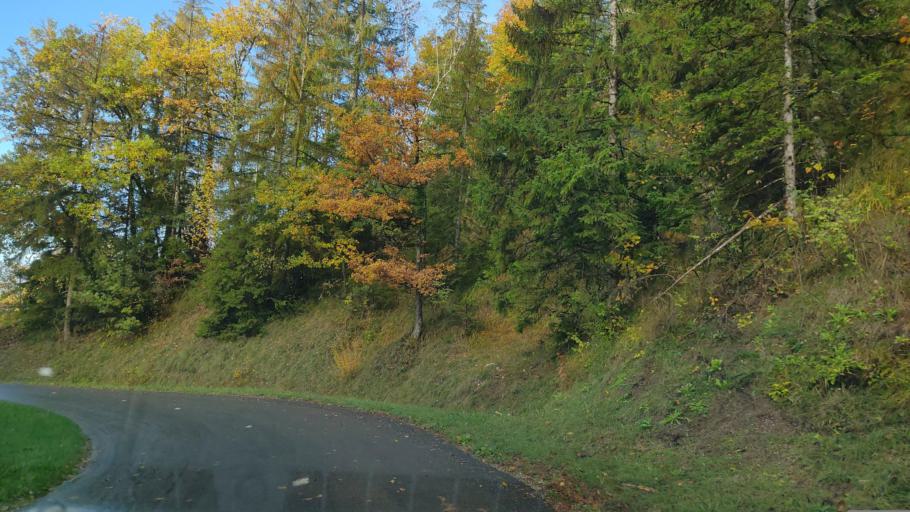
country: FR
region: Rhone-Alpes
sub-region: Departement de la Savoie
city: Novalaise
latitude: 45.6054
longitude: 5.7860
